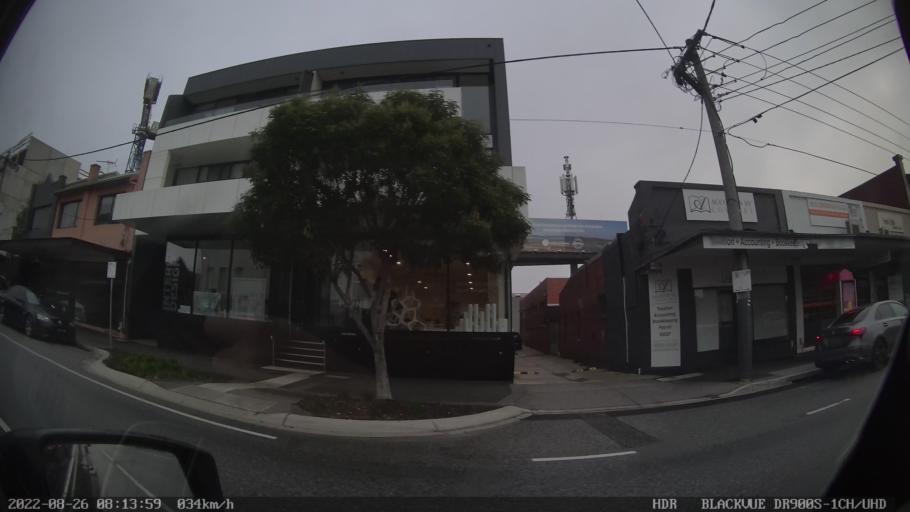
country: AU
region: Victoria
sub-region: Bayside
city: North Brighton
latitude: -37.8981
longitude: 145.0071
